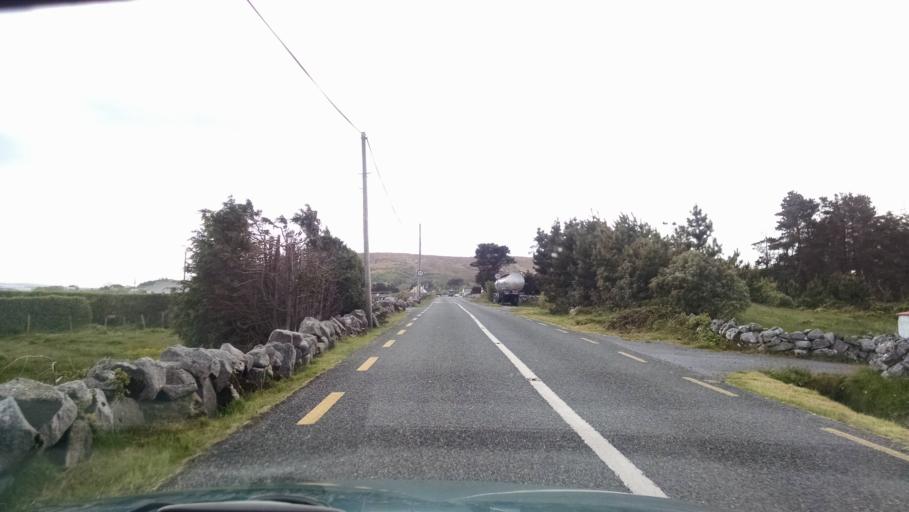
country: IE
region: Connaught
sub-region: County Galway
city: Clifden
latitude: 53.3303
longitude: -9.7305
